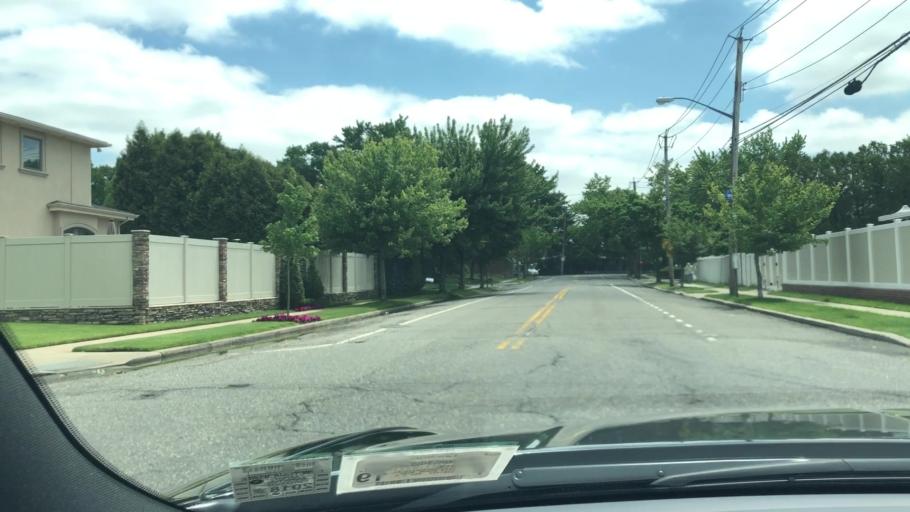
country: US
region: New York
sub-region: Richmond County
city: Staten Island
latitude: 40.5675
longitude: -74.1337
